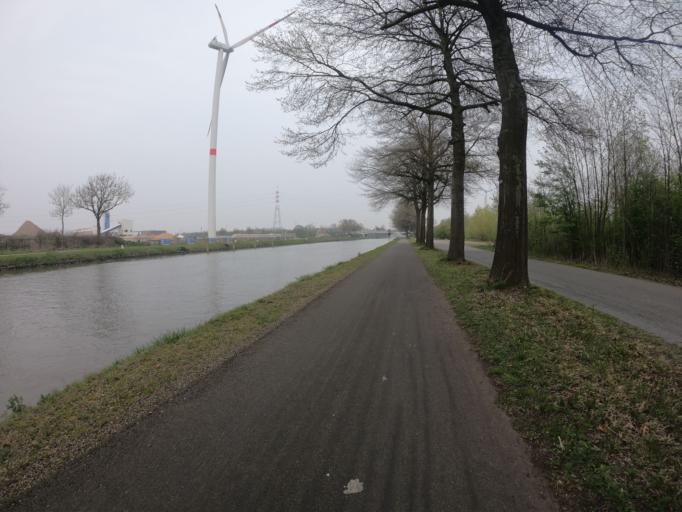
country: BE
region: Flanders
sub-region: Provincie Limburg
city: Maasmechelen
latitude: 50.9483
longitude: 5.7107
